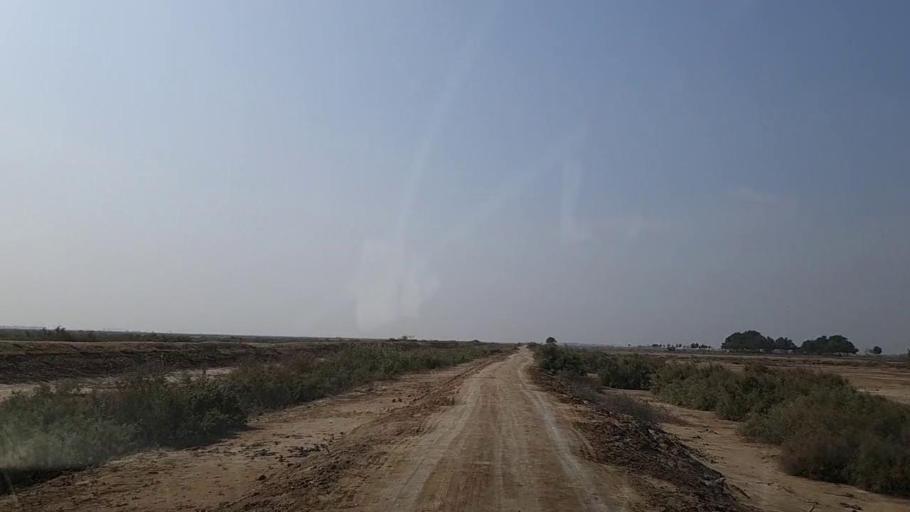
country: PK
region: Sindh
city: Gharo
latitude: 24.6738
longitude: 67.7244
